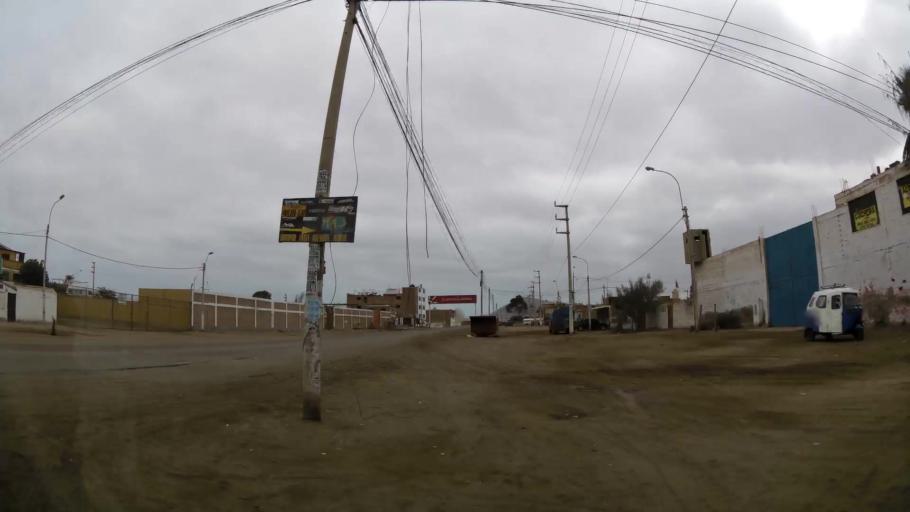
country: PE
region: Lima
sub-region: Provincia de Canete
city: Chilca
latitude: -12.5110
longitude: -76.7375
